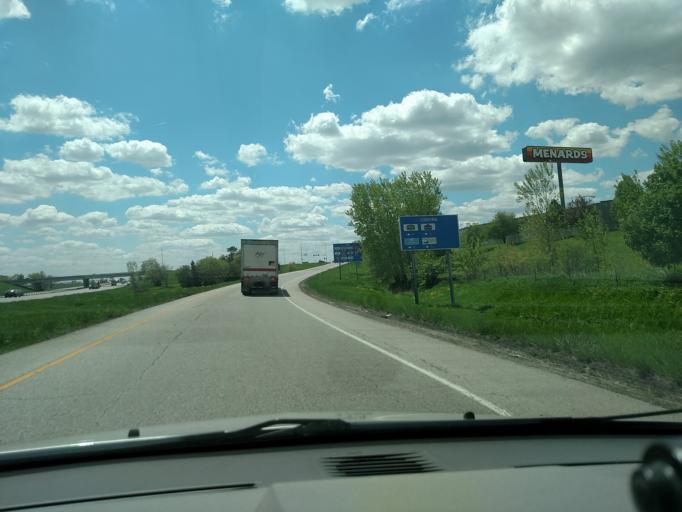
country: US
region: Iowa
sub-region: Polk County
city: Ankeny
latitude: 41.7061
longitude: -93.5766
